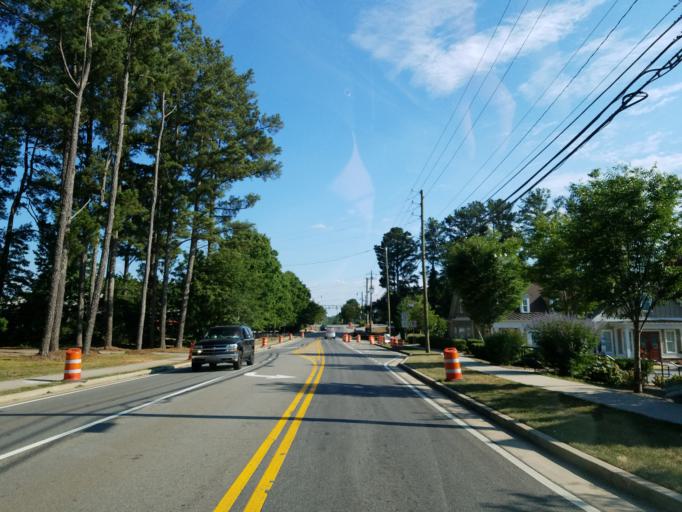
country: US
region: Georgia
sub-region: Fulton County
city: Alpharetta
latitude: 34.0917
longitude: -84.3395
